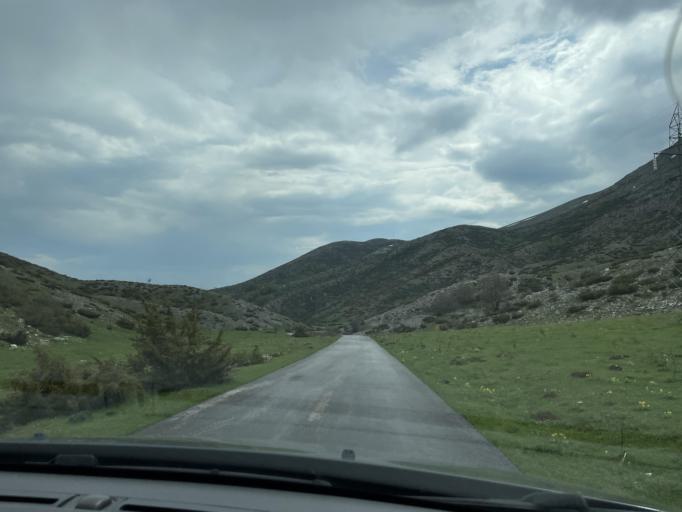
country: MK
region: Opstina Rostusa
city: Rostusha
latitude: 41.6173
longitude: 20.6837
